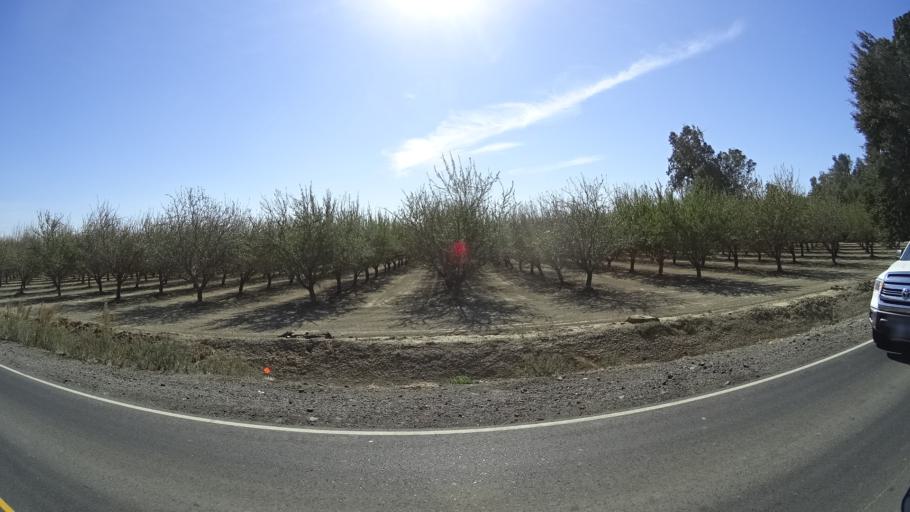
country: US
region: California
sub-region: Yolo County
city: Woodland
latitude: 38.6197
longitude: -121.8160
